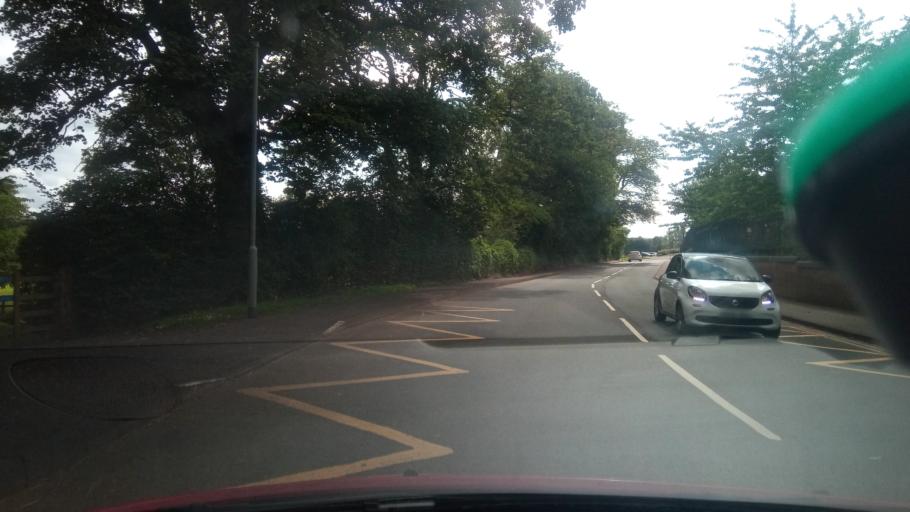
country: GB
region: Scotland
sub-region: East Lothian
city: Ormiston
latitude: 55.9117
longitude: -2.9398
